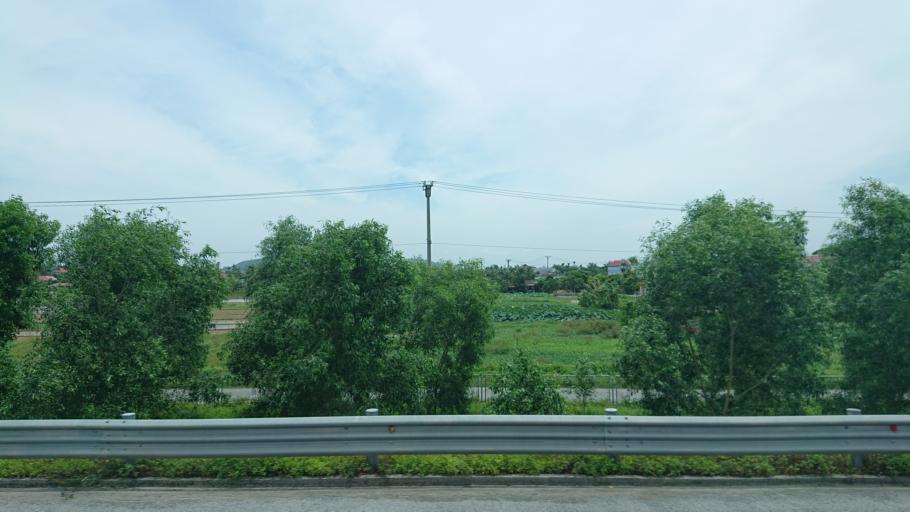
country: VN
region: Hai Phong
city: Nui Doi
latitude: 20.7685
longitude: 106.6333
